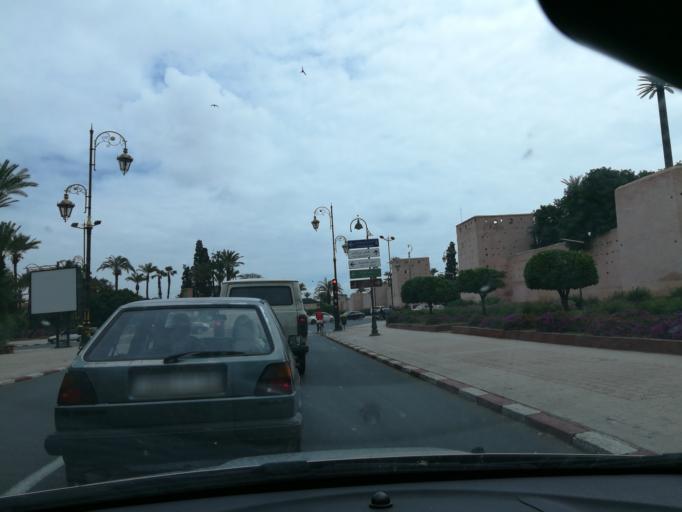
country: MA
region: Marrakech-Tensift-Al Haouz
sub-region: Marrakech
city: Marrakesh
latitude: 31.6281
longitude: -8.0016
